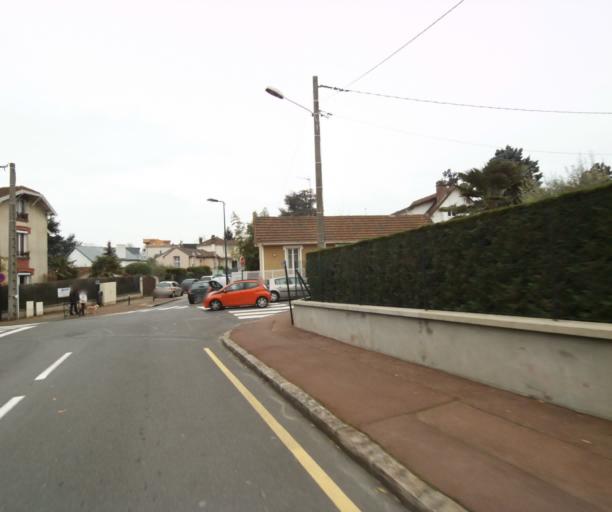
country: FR
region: Ile-de-France
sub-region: Departement des Hauts-de-Seine
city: Garches
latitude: 48.8485
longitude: 2.1905
